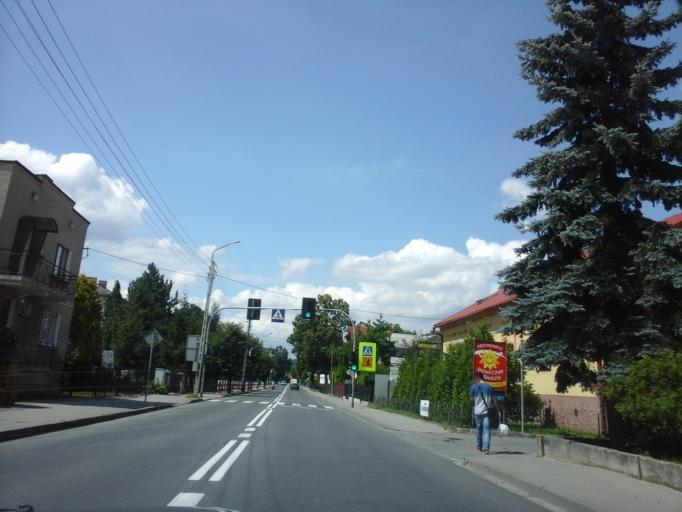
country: PL
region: Lesser Poland Voivodeship
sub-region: Powiat suski
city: Makow Podhalanski
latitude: 49.7302
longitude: 19.6706
